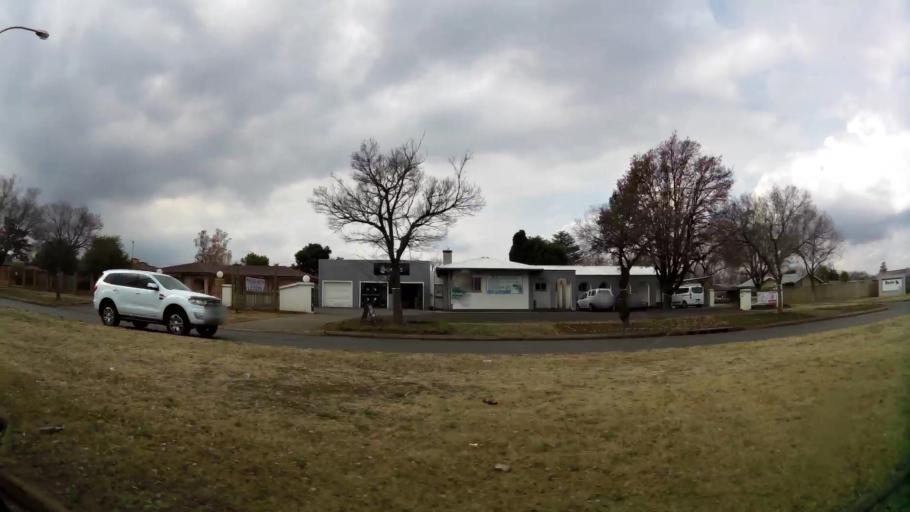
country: ZA
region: Gauteng
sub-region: Sedibeng District Municipality
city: Vanderbijlpark
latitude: -26.7188
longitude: 27.8243
